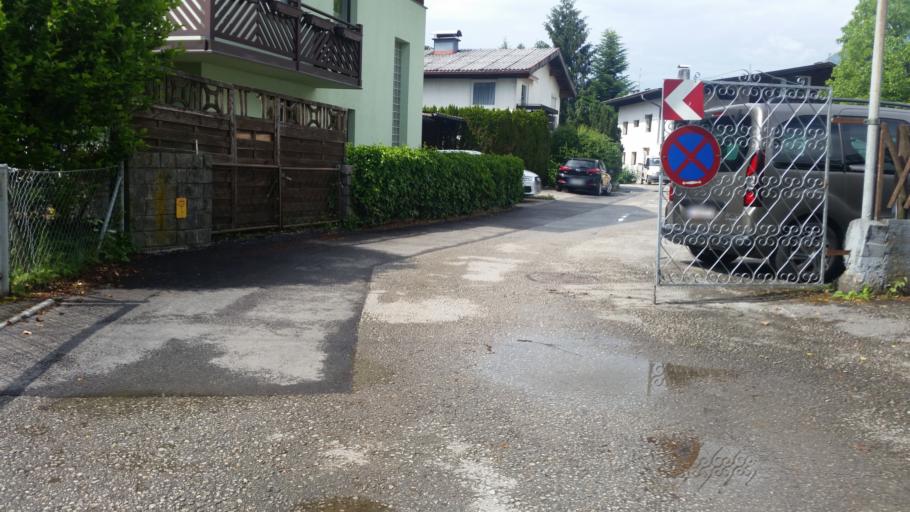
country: AT
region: Salzburg
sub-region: Politischer Bezirk Salzburg-Umgebung
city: Elsbethen
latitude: 47.7729
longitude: 13.0782
